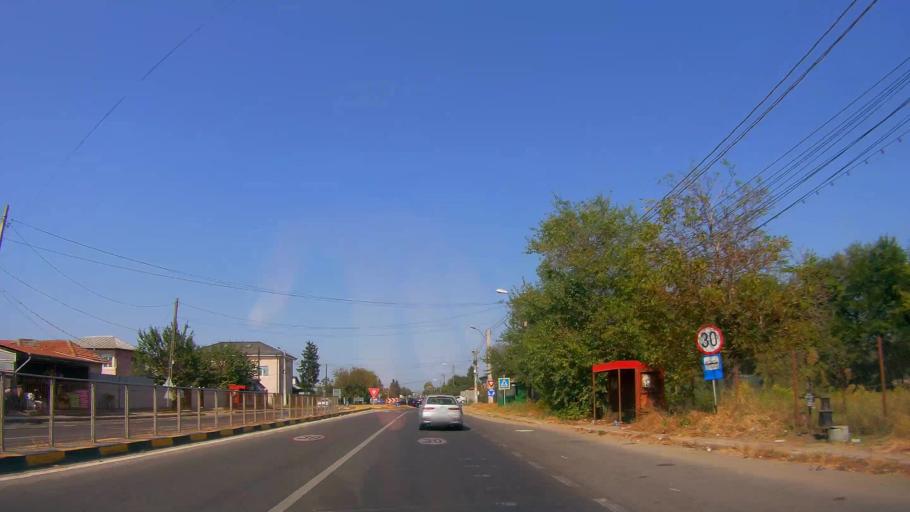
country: RO
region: Giurgiu
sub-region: Comuna Fratesti
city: Remus
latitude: 43.9369
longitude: 25.9774
